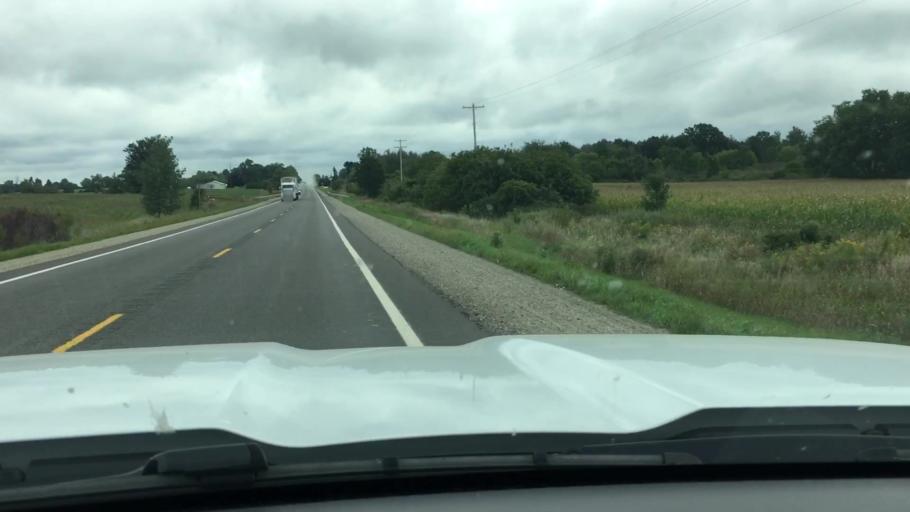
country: US
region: Michigan
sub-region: Montcalm County
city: Carson City
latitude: 43.1774
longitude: -84.9541
